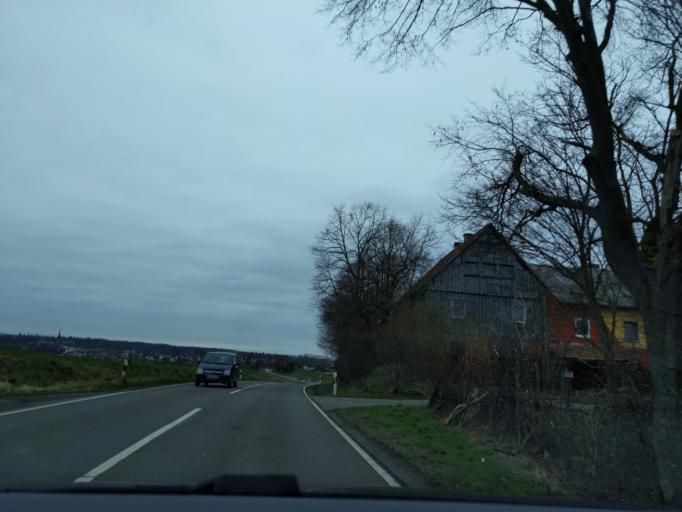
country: DE
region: Hesse
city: Frankenberg
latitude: 51.0442
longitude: 8.8188
